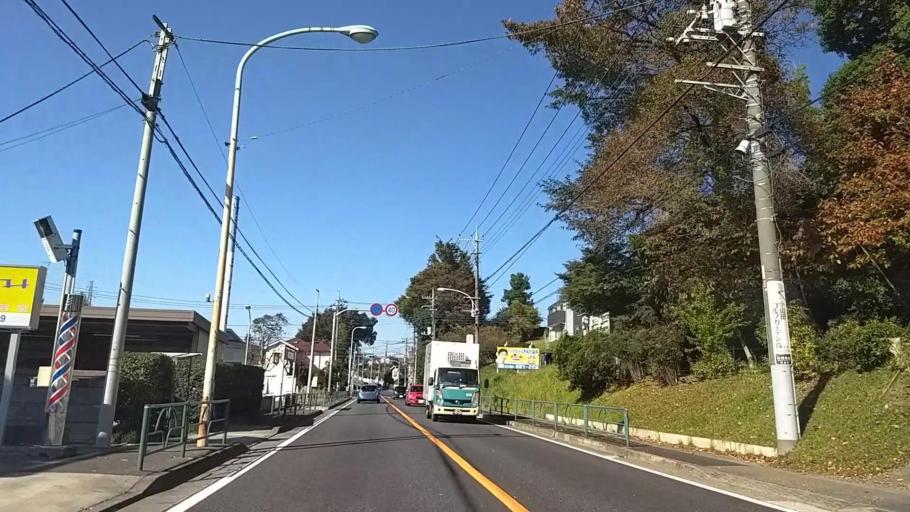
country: JP
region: Tokyo
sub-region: Machida-shi
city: Machida
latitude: 35.5843
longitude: 139.4009
